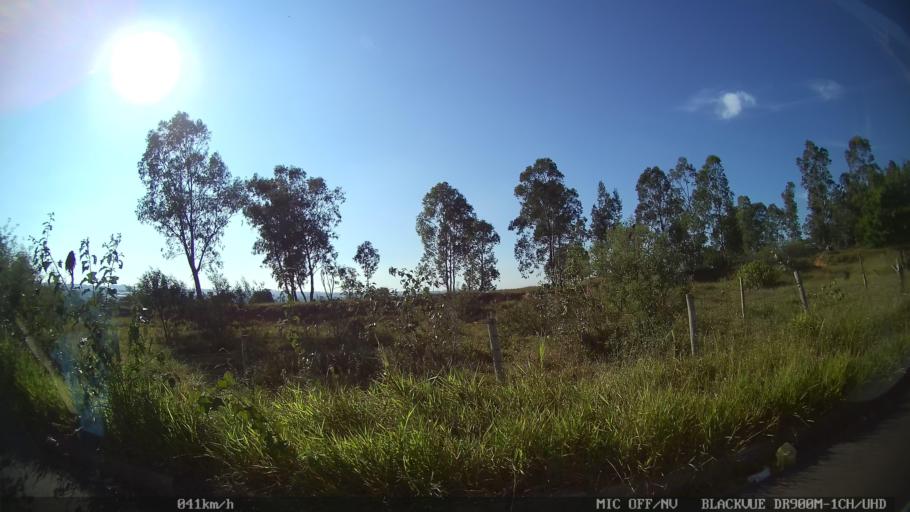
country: BR
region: Sao Paulo
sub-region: Campinas
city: Campinas
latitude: -22.9717
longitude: -47.1104
